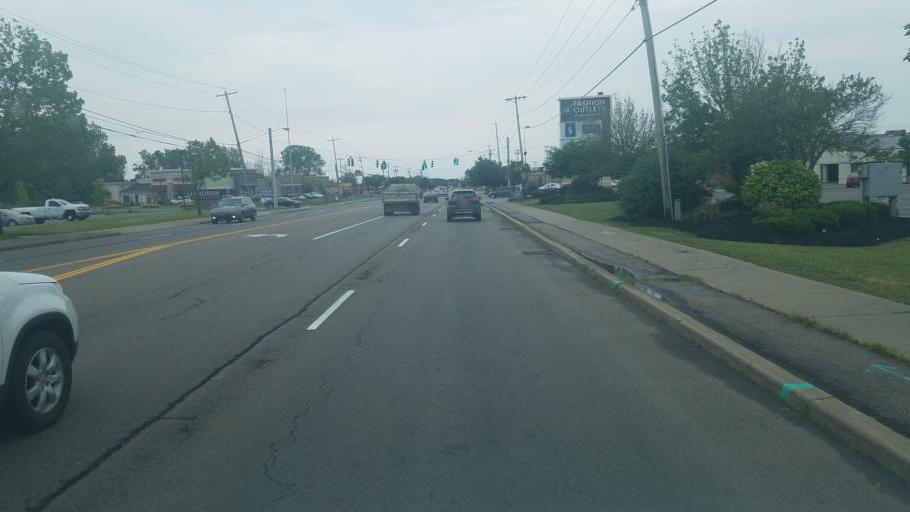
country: US
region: New York
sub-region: Niagara County
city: Niagara Falls
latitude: 43.0980
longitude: -78.9758
